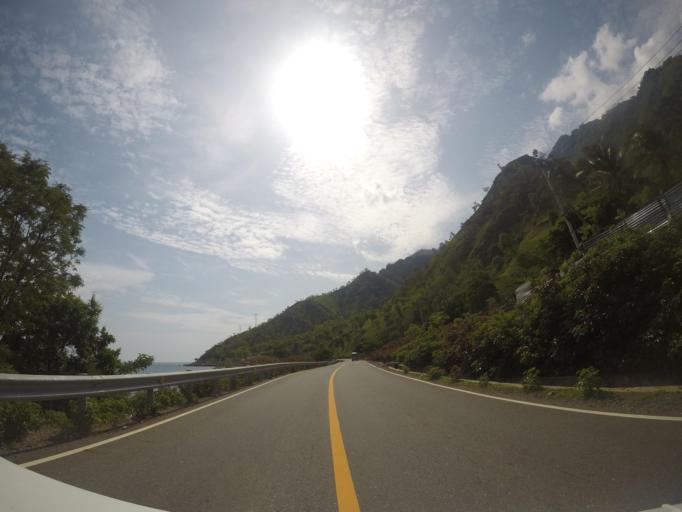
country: TL
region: Manatuto
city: Manatuto
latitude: -8.4802
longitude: 125.9227
